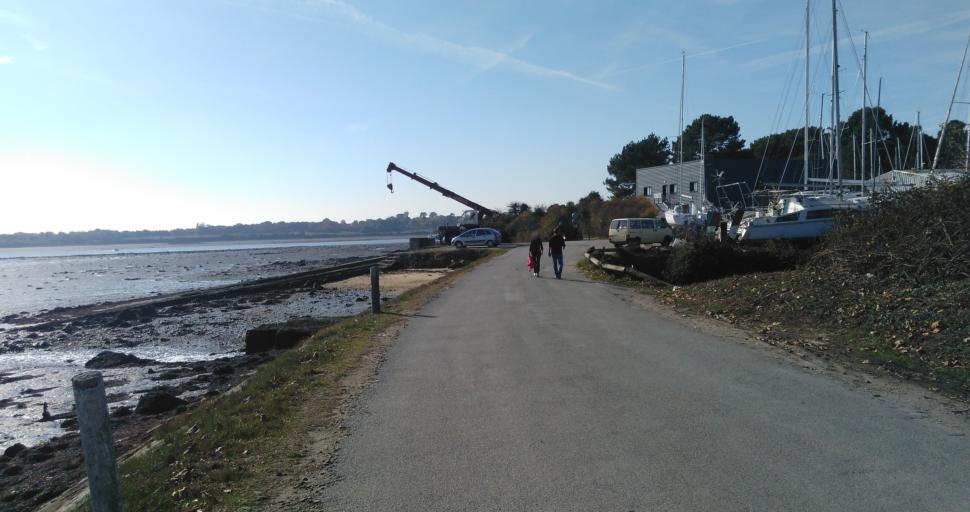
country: FR
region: Brittany
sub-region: Departement du Morbihan
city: Sene
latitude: 47.6326
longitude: -2.7630
